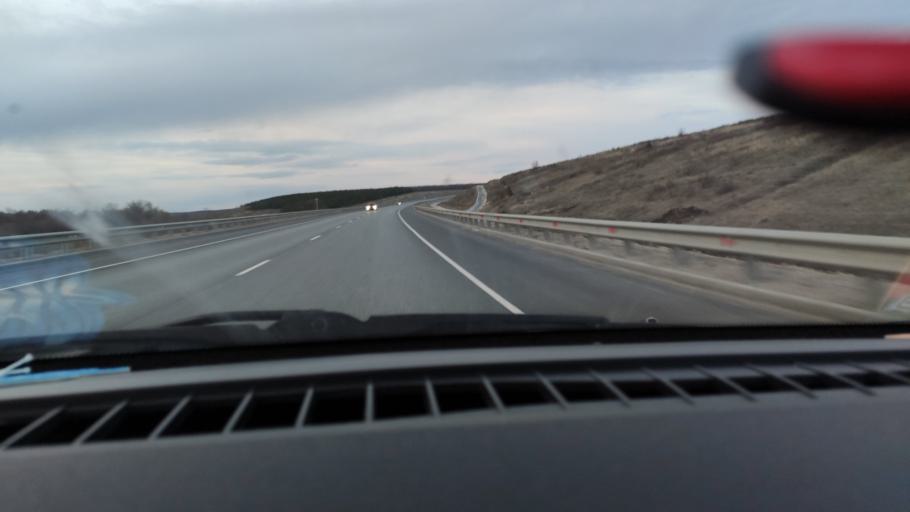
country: RU
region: Saratov
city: Yelshanka
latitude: 51.8741
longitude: 46.5056
